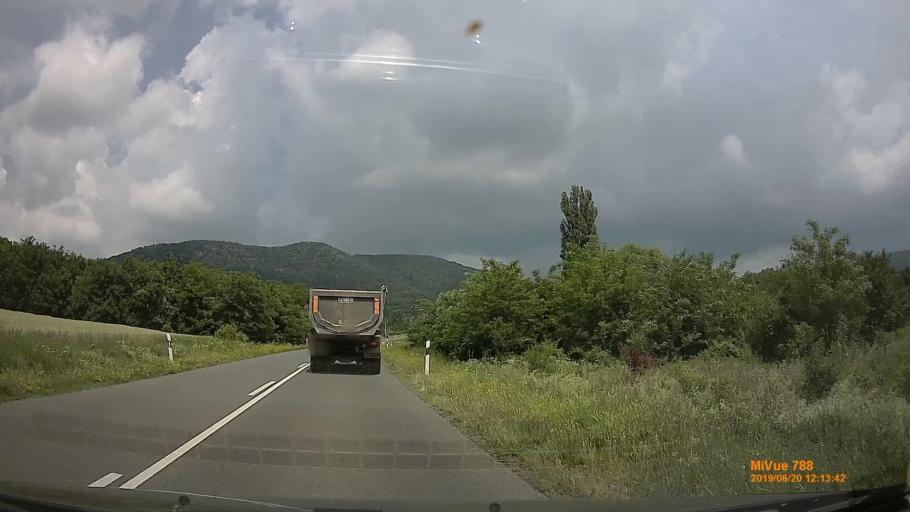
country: HU
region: Baranya
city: Hosszuheteny
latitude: 46.1608
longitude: 18.3426
